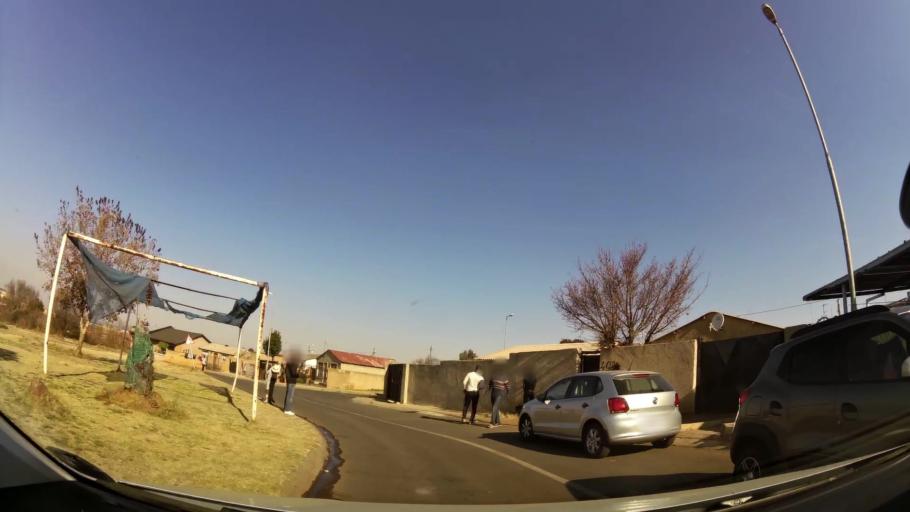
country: ZA
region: Gauteng
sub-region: City of Johannesburg Metropolitan Municipality
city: Soweto
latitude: -26.2786
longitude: 27.8720
